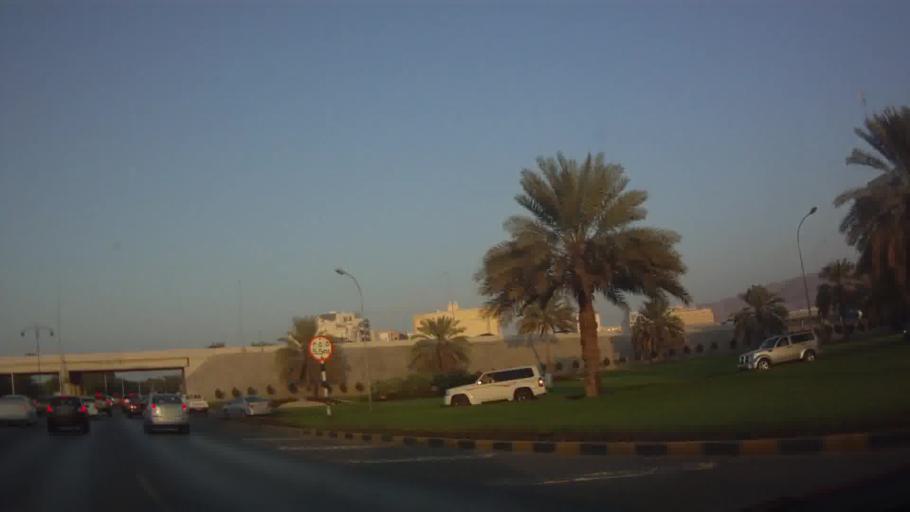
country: OM
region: Muhafazat Masqat
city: Bawshar
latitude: 23.5954
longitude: 58.4128
